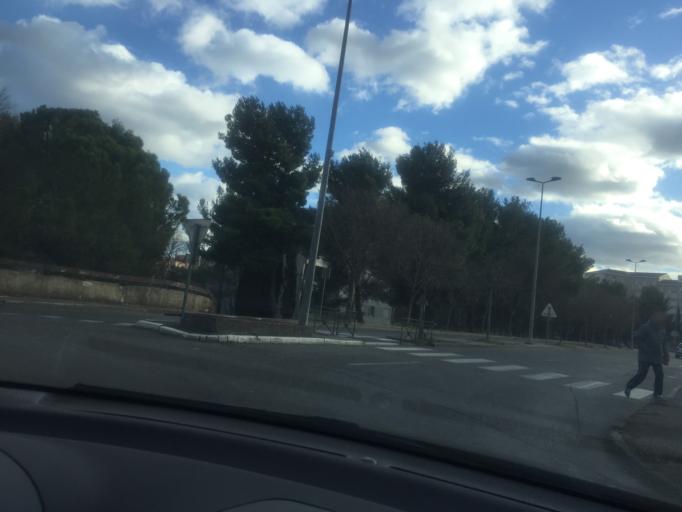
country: FR
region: Provence-Alpes-Cote d'Azur
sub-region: Departement des Bouches-du-Rhone
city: Aix-en-Provence
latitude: 43.5286
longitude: 5.4160
